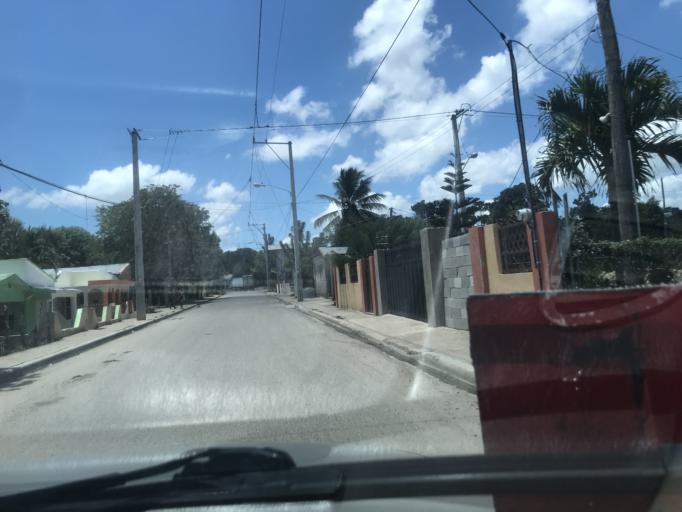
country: DO
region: Santiago
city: Santiago de los Caballeros
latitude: 19.4043
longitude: -70.6813
